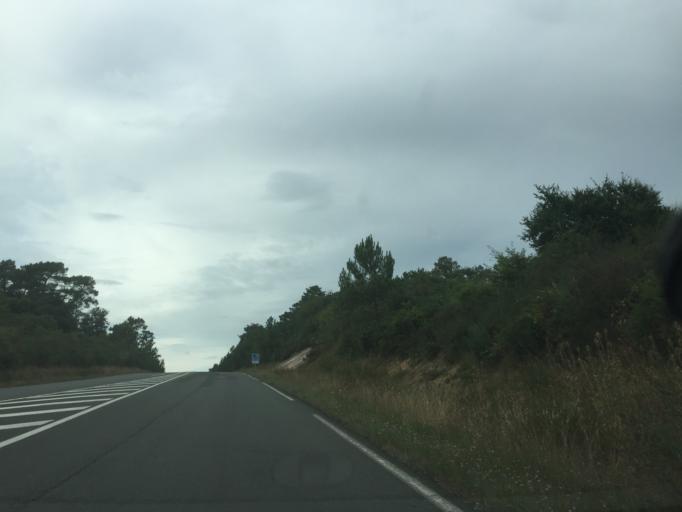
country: FR
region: Aquitaine
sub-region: Departement du Lot-et-Garonne
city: Fumel
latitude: 44.5247
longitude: 0.9484
